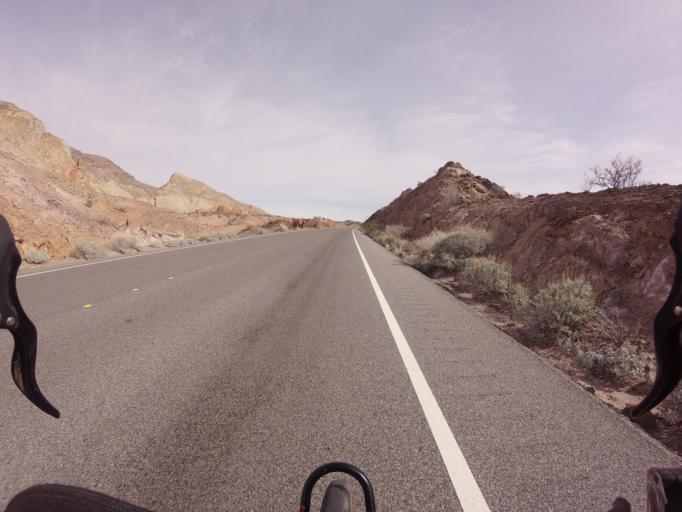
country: US
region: Nevada
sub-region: Clark County
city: Boulder City
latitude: 36.1952
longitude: -114.7102
